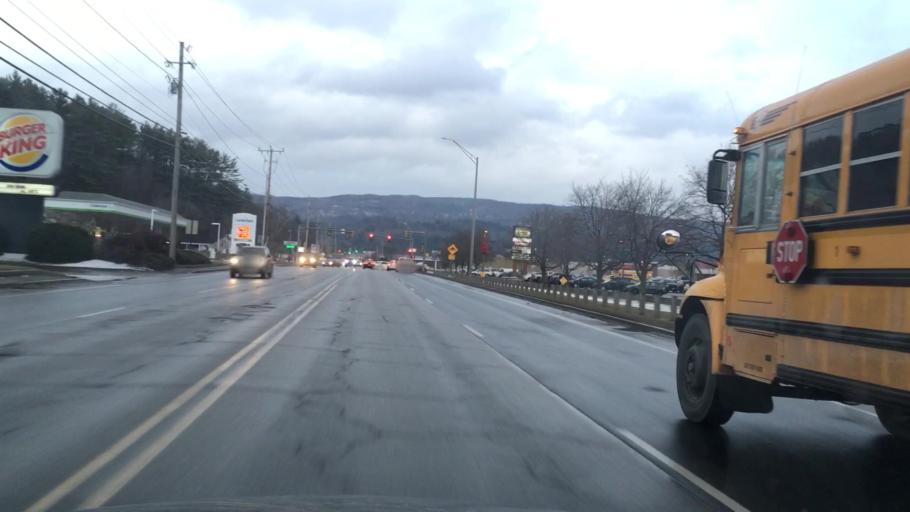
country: US
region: New Hampshire
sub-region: Sullivan County
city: Claremont
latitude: 43.3656
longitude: -72.3204
